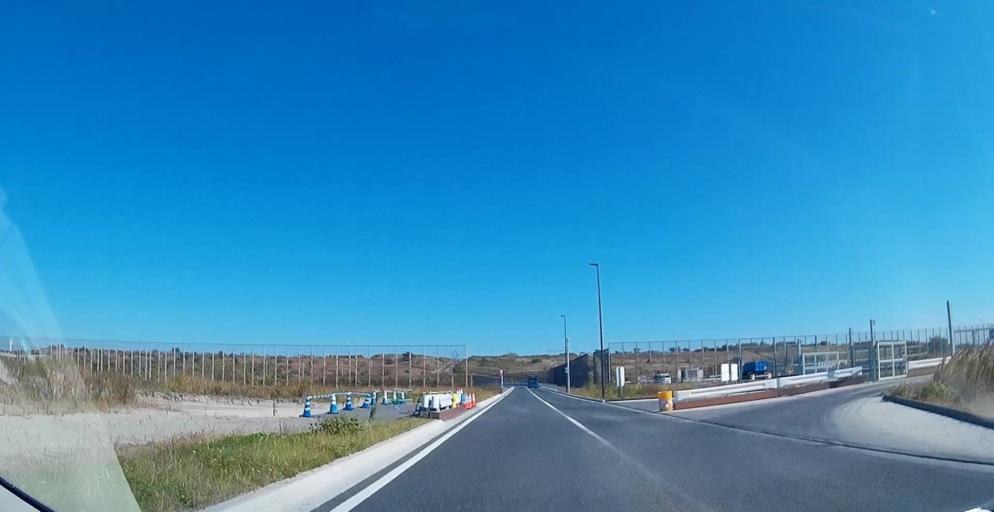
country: JP
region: Tokyo
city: Urayasu
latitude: 35.5926
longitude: 139.8076
